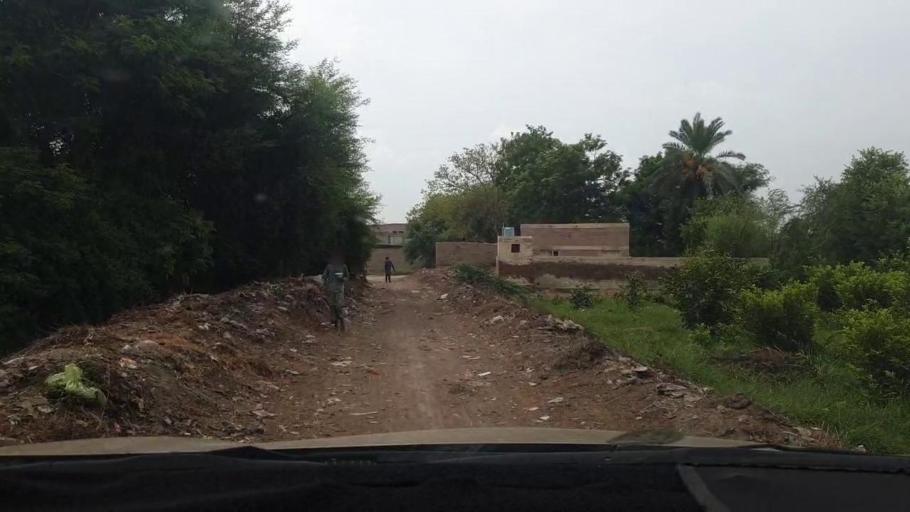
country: PK
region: Sindh
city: Naudero
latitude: 27.6304
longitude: 68.3100
